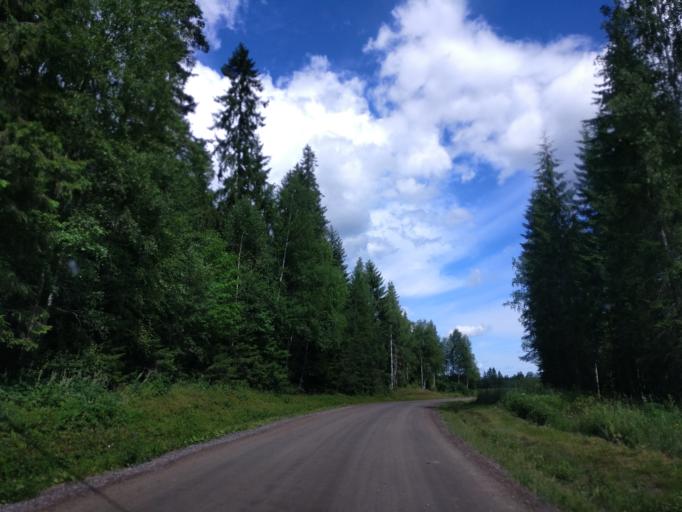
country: SE
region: Vaermland
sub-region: Hagfors Kommun
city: Ekshaerad
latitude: 60.0568
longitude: 13.4772
